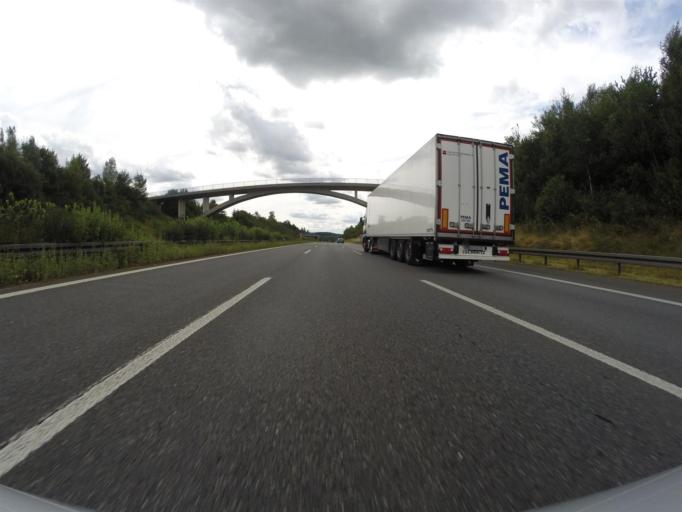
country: DE
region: Bavaria
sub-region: Upper Franconia
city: Marktschorgast
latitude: 50.0800
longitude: 11.6616
